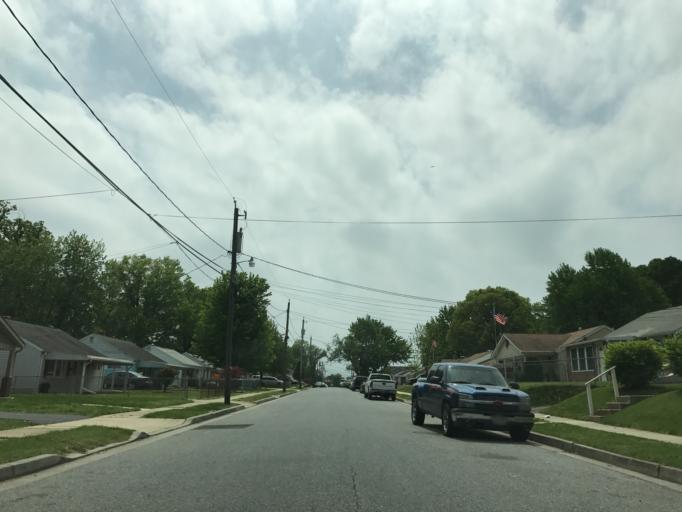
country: US
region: Maryland
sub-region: Baltimore County
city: Middle River
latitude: 39.3117
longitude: -76.4426
